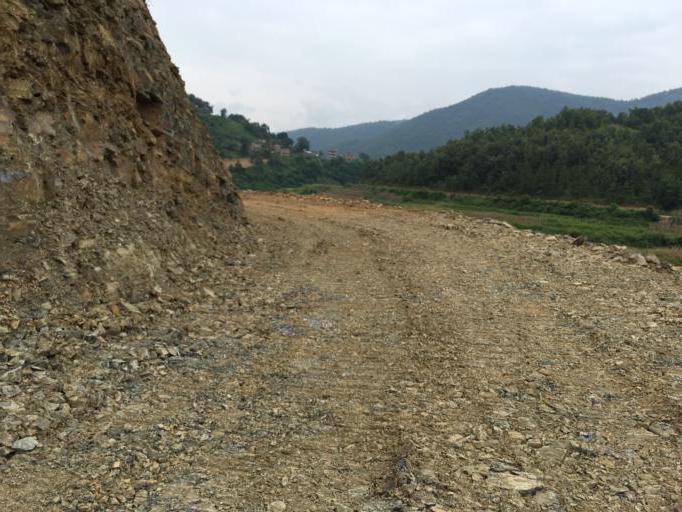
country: CN
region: Guangxi Zhuangzu Zizhiqu
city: Tongle
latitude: 25.1246
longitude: 106.4184
